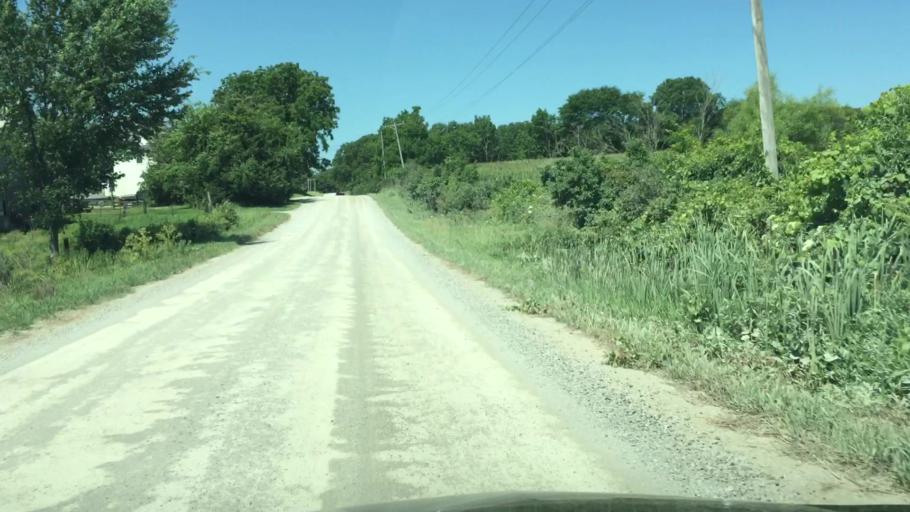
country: US
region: Iowa
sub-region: Linn County
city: Ely
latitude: 41.8329
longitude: -91.5821
